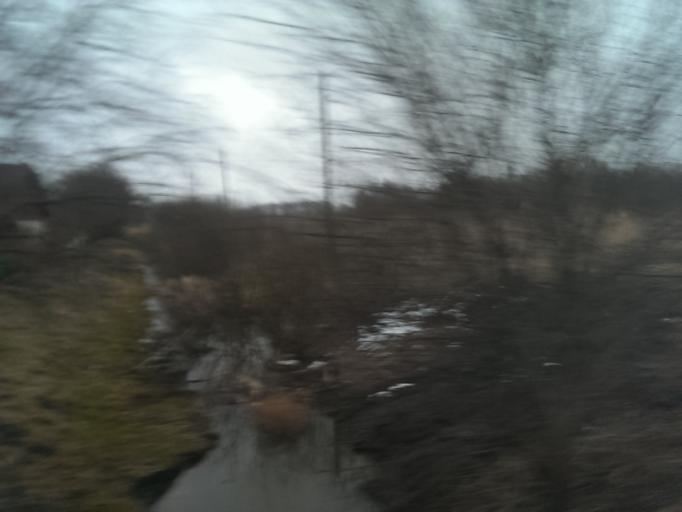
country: LV
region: Ventspils
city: Ventspils
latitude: 57.3602
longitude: 21.6243
